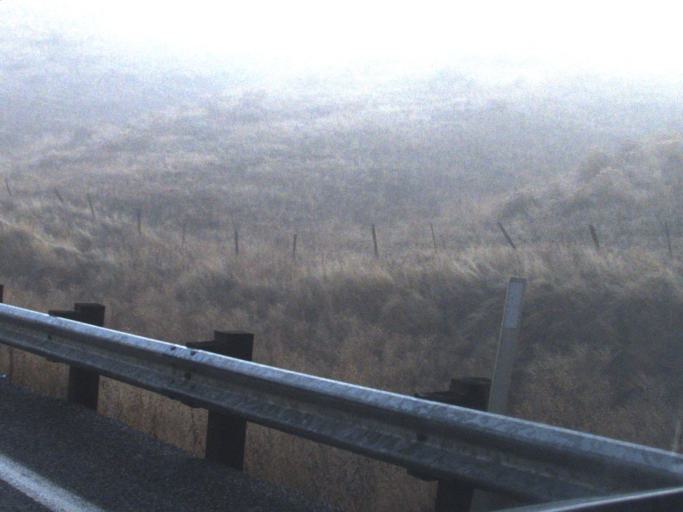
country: US
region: Washington
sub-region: Asotin County
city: Clarkston Heights-Vineland
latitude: 46.4330
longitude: -117.3341
